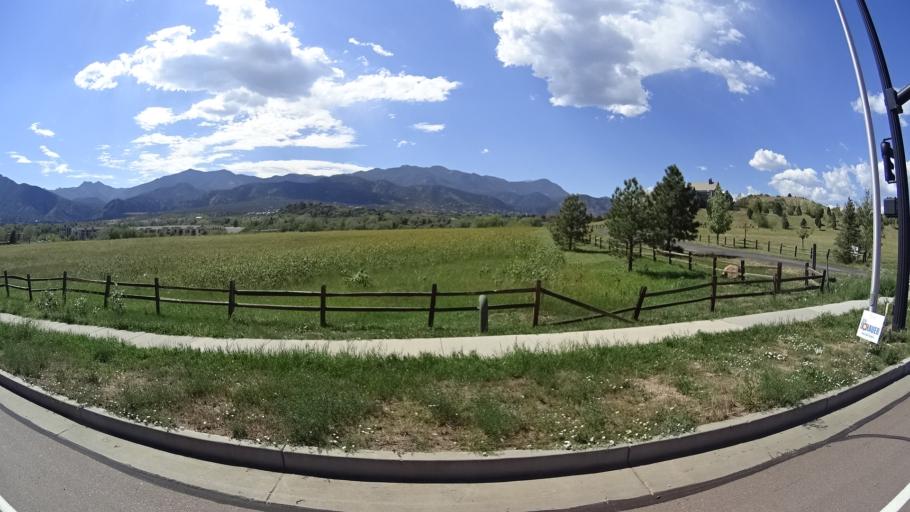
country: US
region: Colorado
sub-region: El Paso County
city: Colorado Springs
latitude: 38.8127
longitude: -104.8409
